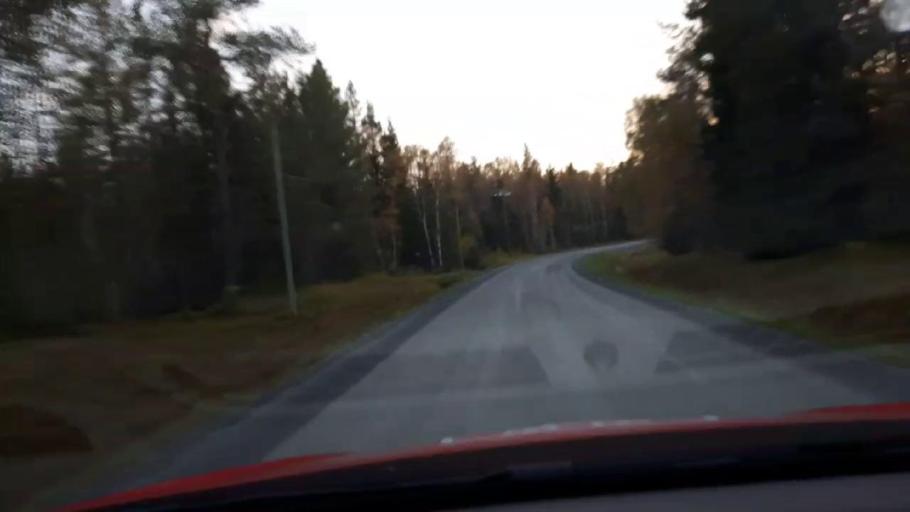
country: SE
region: Jaemtland
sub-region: OEstersunds Kommun
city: Ostersund
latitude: 63.2764
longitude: 14.6452
